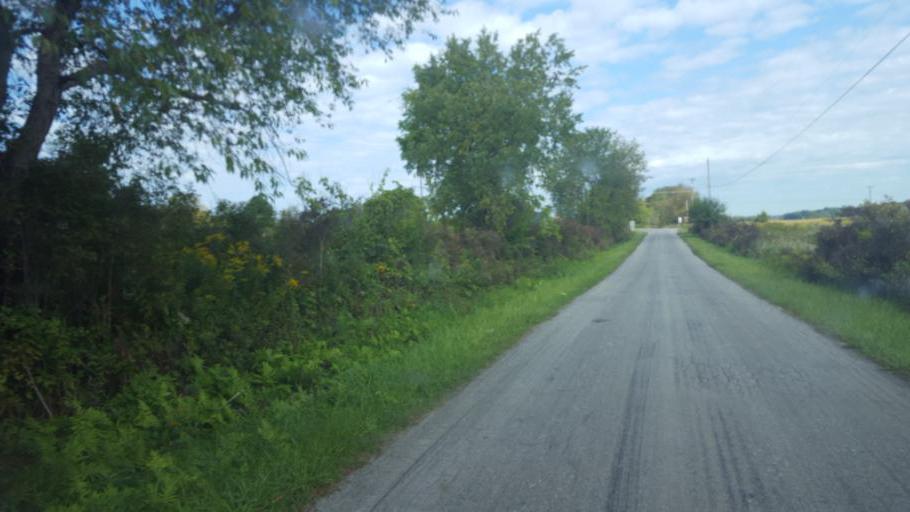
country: US
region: Pennsylvania
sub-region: Mercer County
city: Greenville
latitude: 41.5105
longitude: -80.3654
